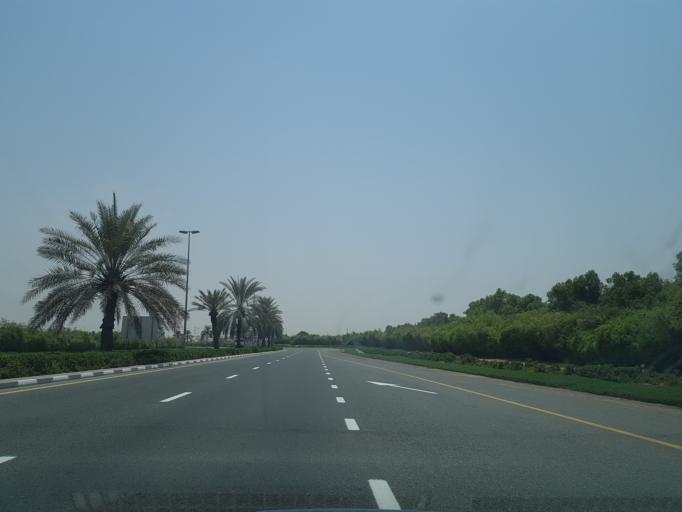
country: AE
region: Ash Shariqah
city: Sharjah
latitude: 25.1117
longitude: 55.3947
